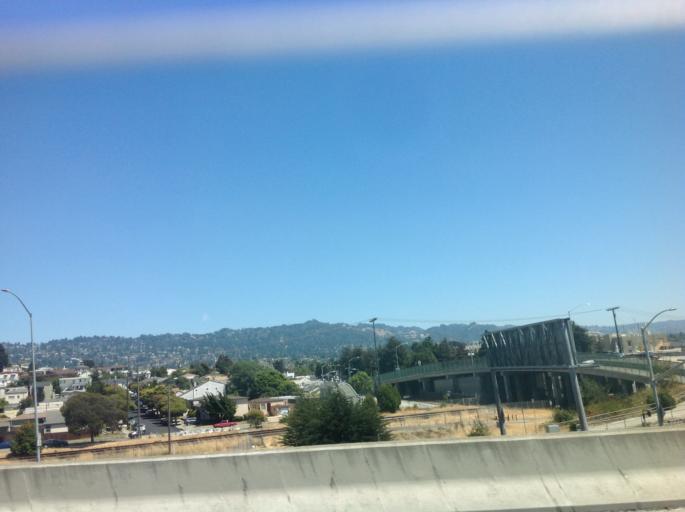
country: US
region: California
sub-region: Alameda County
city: Albany
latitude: 37.8878
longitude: -122.3087
